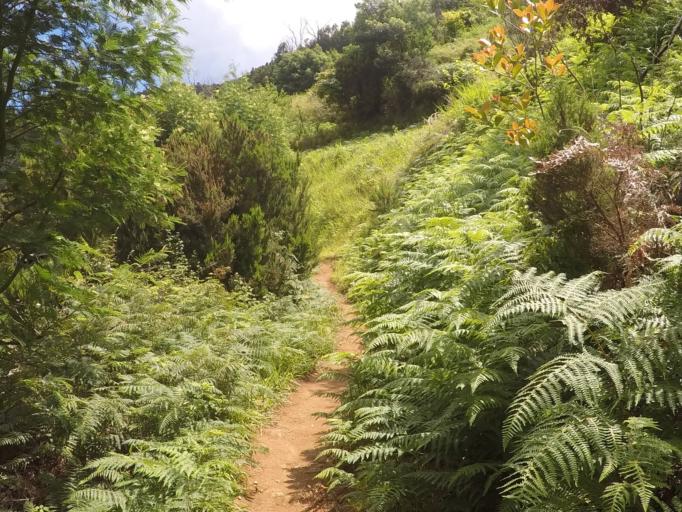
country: PT
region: Madeira
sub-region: Machico
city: Canical
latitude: 32.7493
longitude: -16.7725
